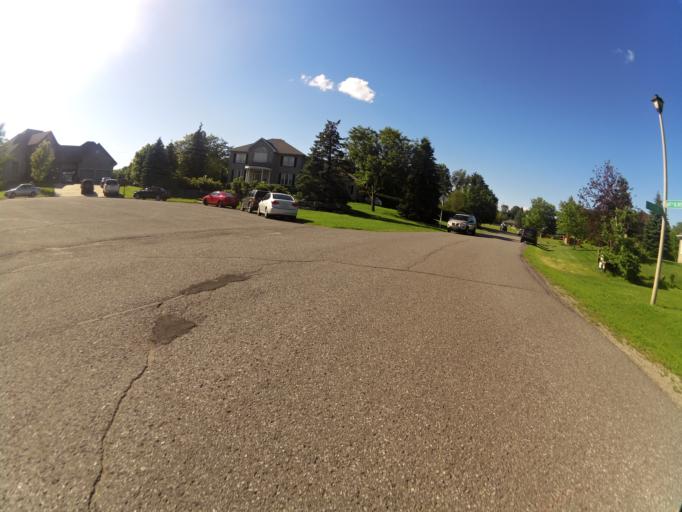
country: CA
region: Ontario
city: Bells Corners
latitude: 45.2628
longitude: -75.8259
